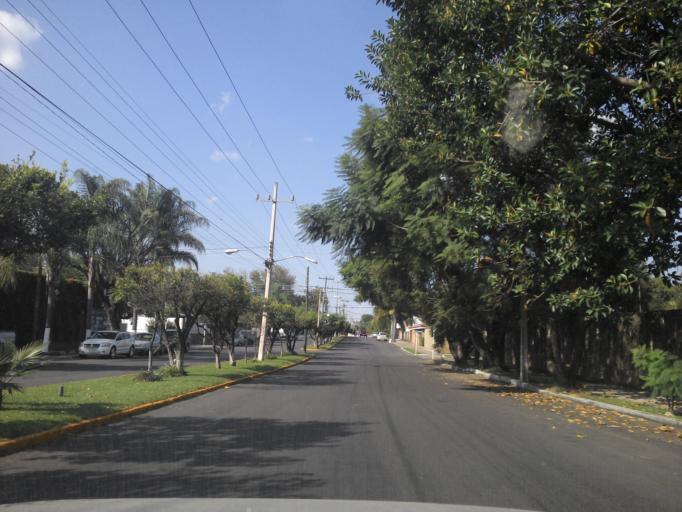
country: MX
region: Jalisco
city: Guadalajara
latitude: 20.6549
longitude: -103.4083
